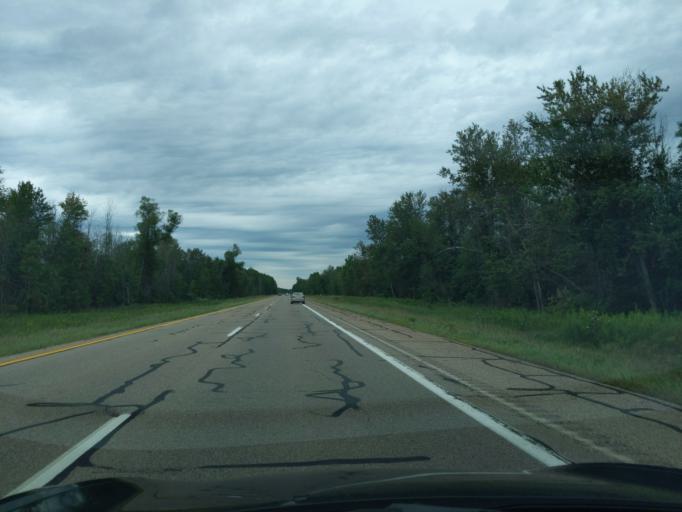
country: US
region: Michigan
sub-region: Roscommon County
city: Houghton Lake
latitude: 44.2963
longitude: -84.8013
